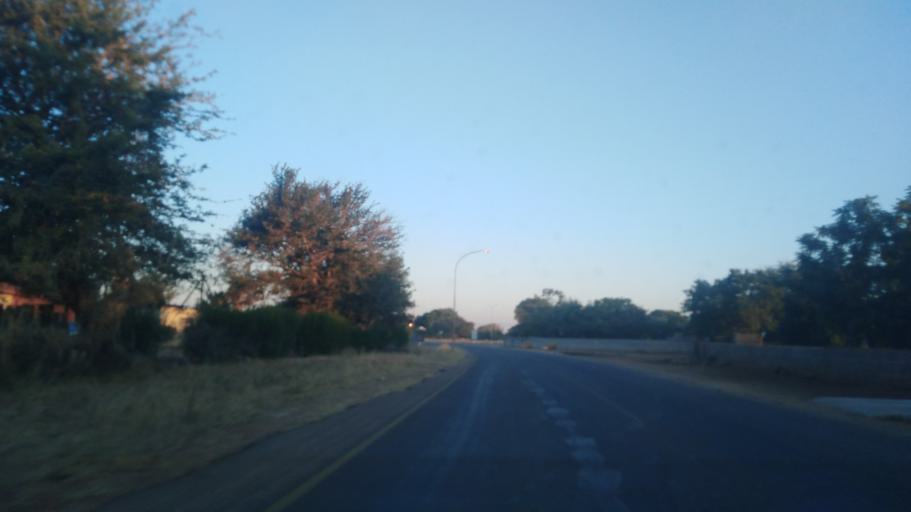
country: BW
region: Central
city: Mahalapye
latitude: -23.1218
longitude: 26.8281
